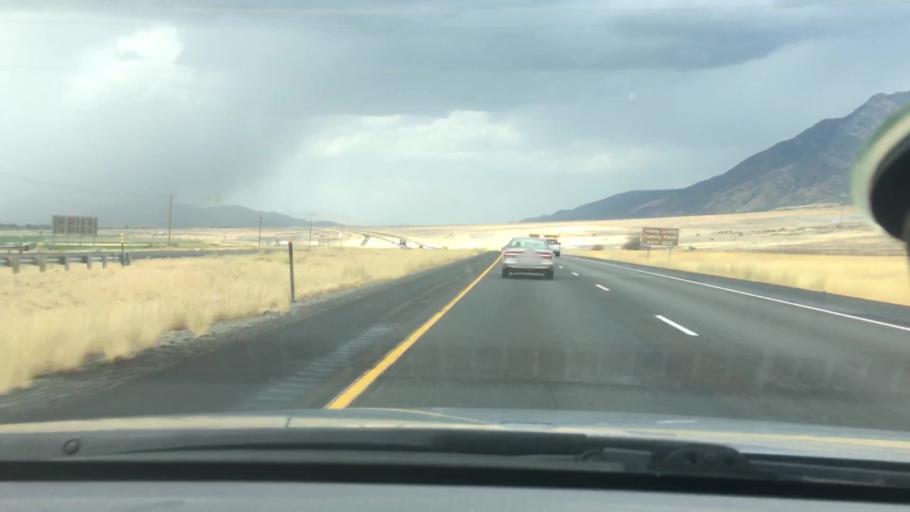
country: US
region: Utah
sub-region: Juab County
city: Mona
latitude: 39.8079
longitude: -111.8351
